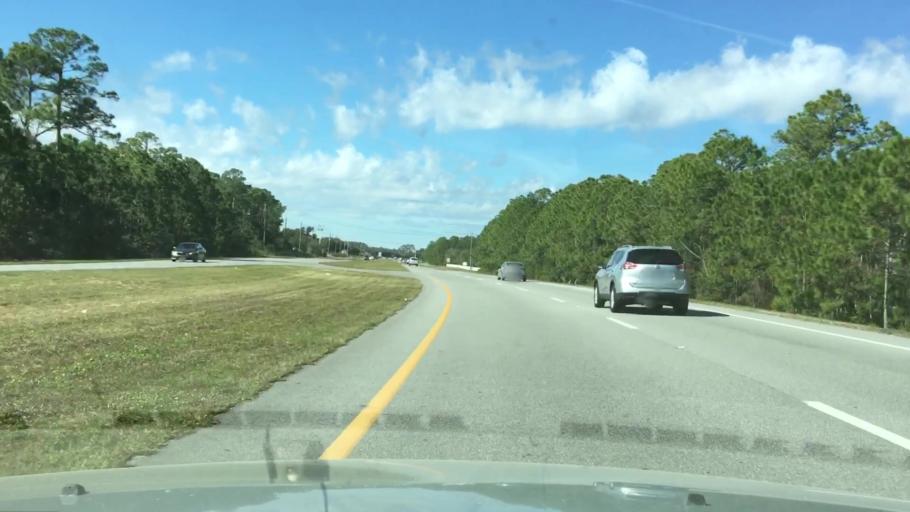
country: US
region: Florida
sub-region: Volusia County
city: South Daytona
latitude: 29.1637
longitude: -81.0705
